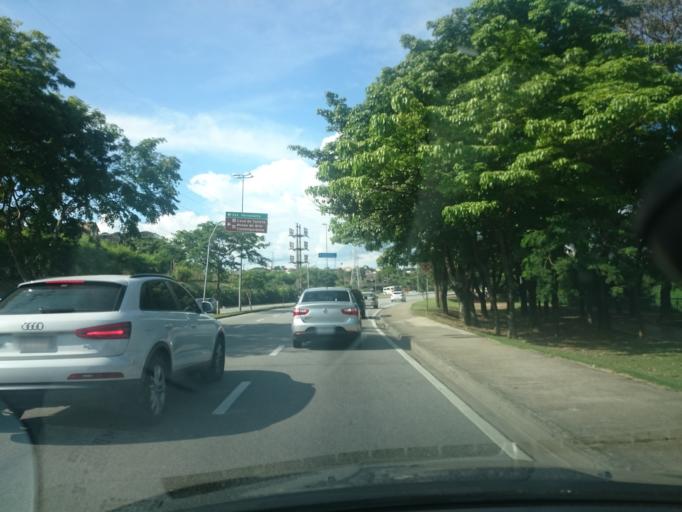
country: BR
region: Sao Paulo
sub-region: Sorocaba
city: Sorocaba
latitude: -23.4998
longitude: -47.4522
